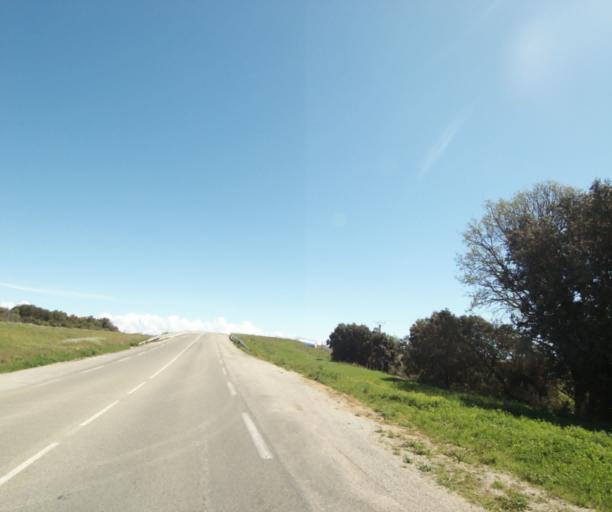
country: FR
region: Languedoc-Roussillon
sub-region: Departement de l'Herault
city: Villeneuve-les-Maguelone
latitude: 43.5565
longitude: 3.8553
